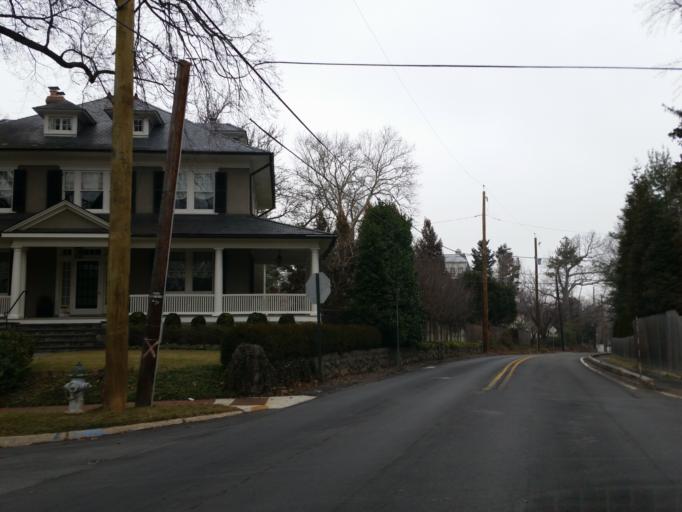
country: US
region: Maryland
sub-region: Montgomery County
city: Chevy Chase
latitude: 38.9748
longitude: -77.0730
